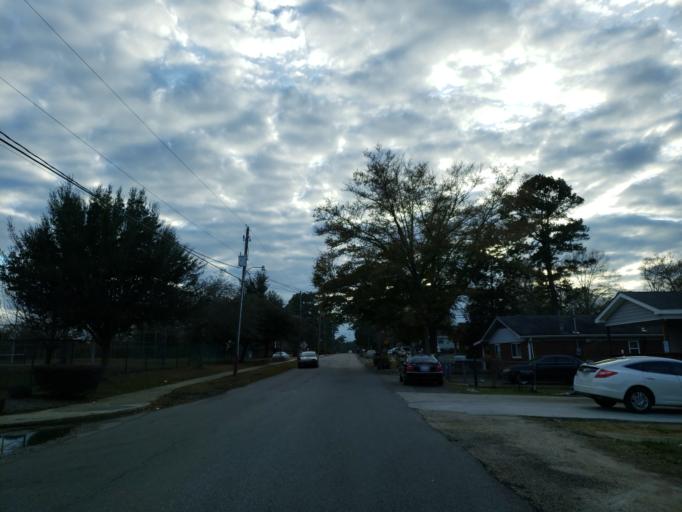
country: US
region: Mississippi
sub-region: Forrest County
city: Hattiesburg
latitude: 31.3074
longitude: -89.3077
